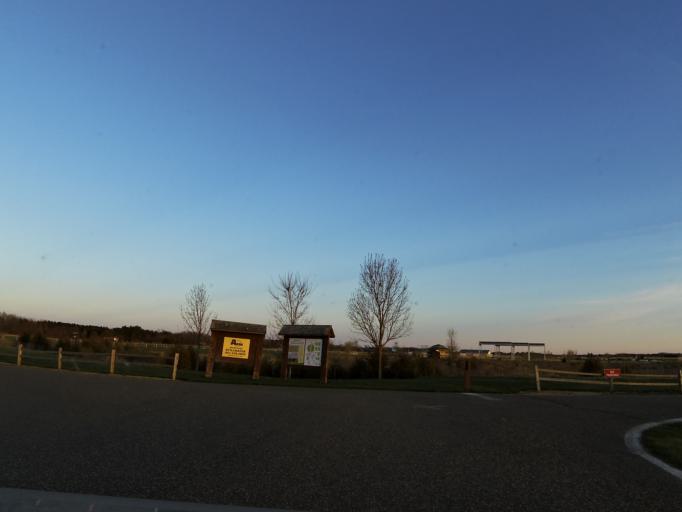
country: US
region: Minnesota
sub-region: Washington County
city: Lakeland
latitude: 44.9558
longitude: -92.7891
